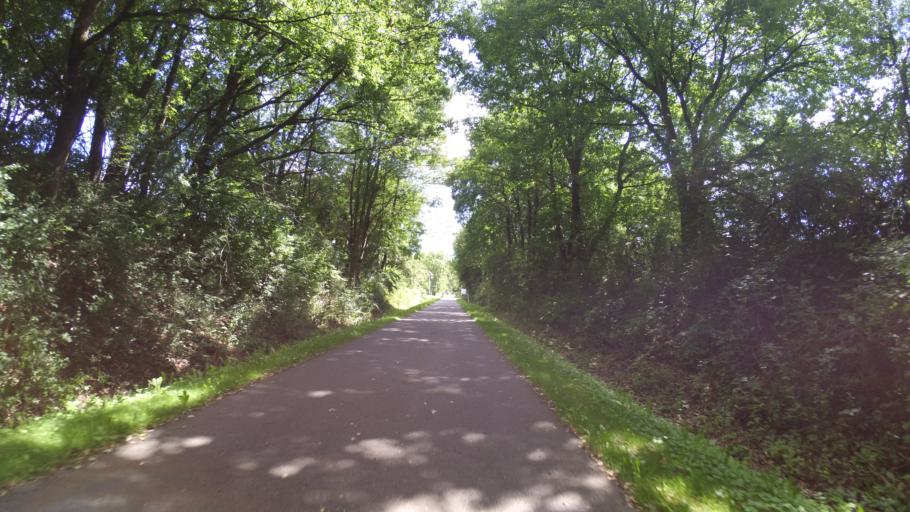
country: DE
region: Saarland
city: Sankt Wendel
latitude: 49.4859
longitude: 7.1520
